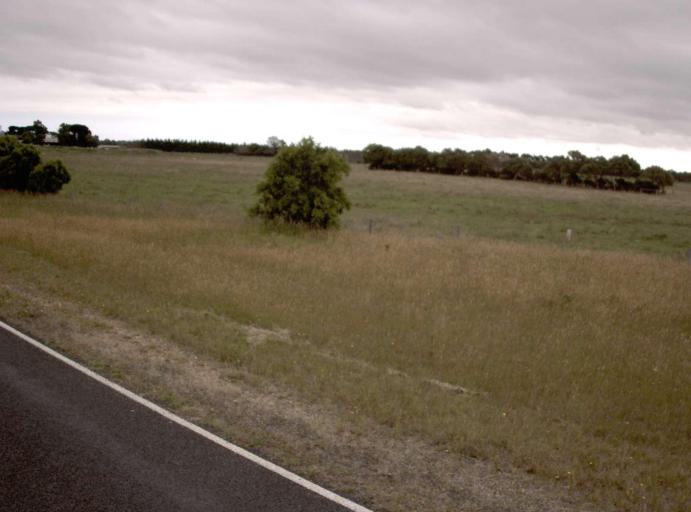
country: AU
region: Victoria
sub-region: Wellington
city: Sale
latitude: -38.5426
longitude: 146.8875
